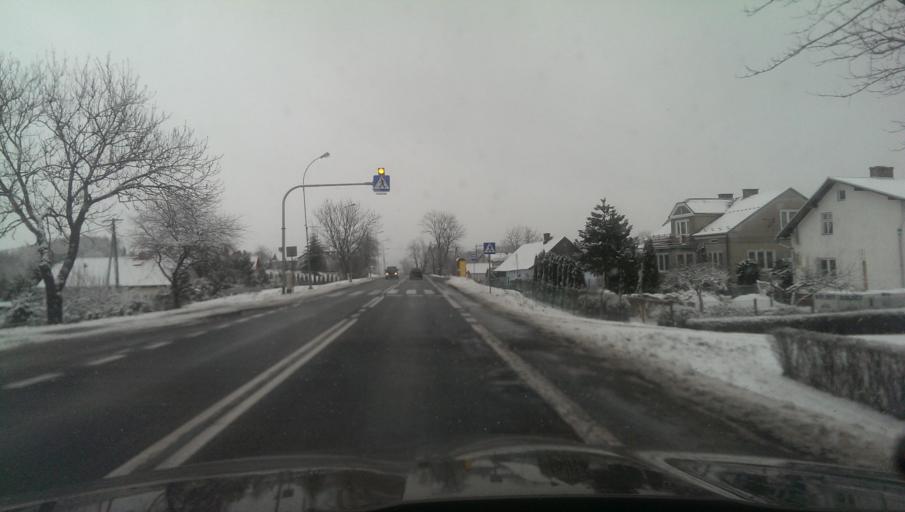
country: PL
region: Subcarpathian Voivodeship
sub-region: Powiat sanocki
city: Besko
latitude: 49.5830
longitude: 21.9385
